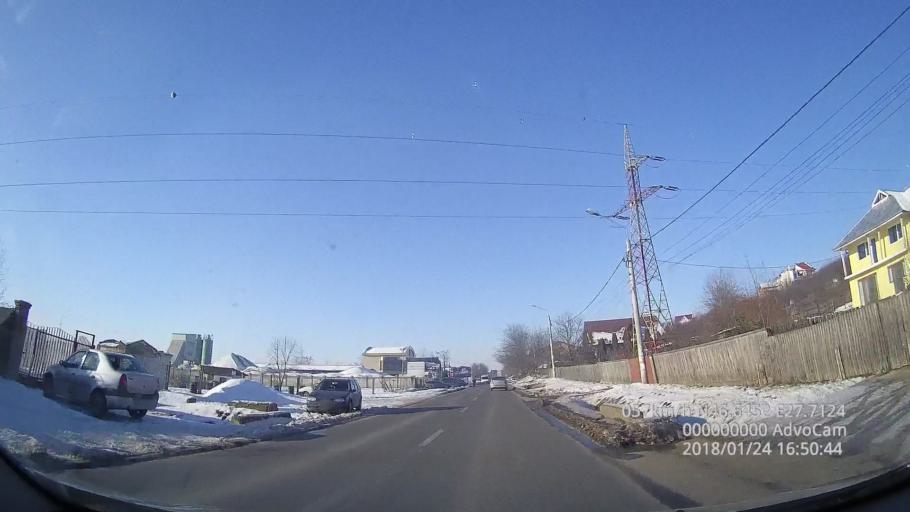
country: RO
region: Vaslui
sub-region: Municipiul Vaslui
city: Rediu
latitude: 46.6454
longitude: 27.7121
